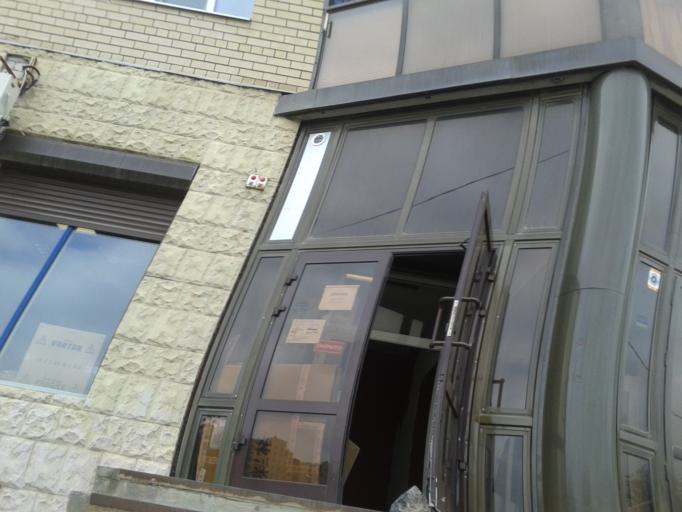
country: RU
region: Volgograd
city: Volgograd
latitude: 48.7489
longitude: 44.5058
